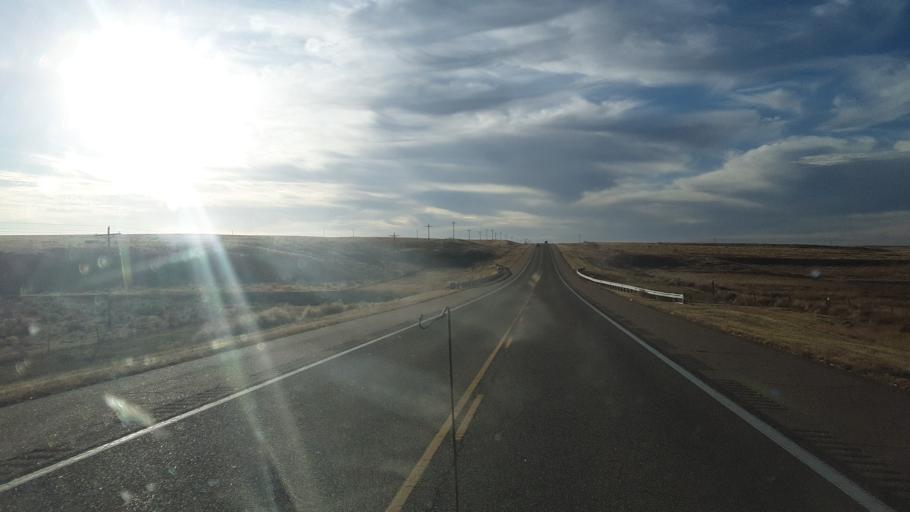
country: US
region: Kansas
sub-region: Kearny County
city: Lakin
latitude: 37.9439
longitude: -101.4424
